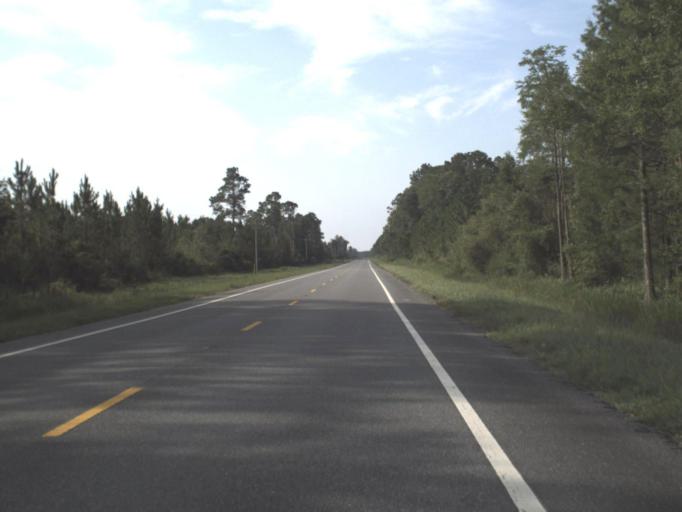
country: US
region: Florida
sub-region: Taylor County
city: Perry
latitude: 30.2390
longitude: -83.6195
